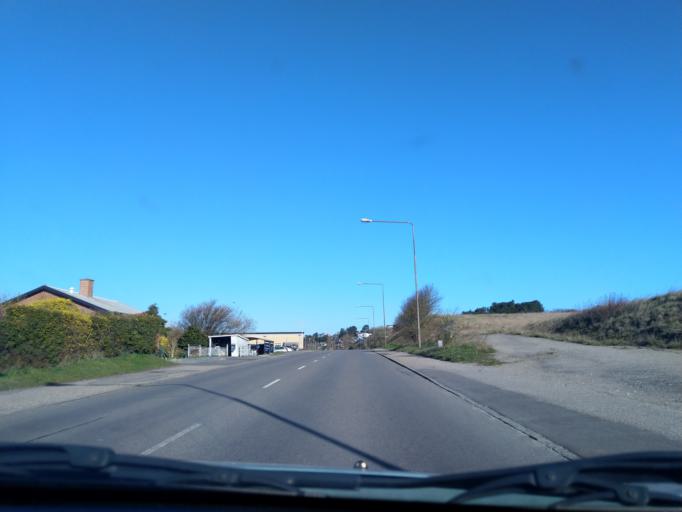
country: DK
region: Zealand
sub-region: Kalundborg Kommune
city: Kalundborg
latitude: 55.6902
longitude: 11.0533
